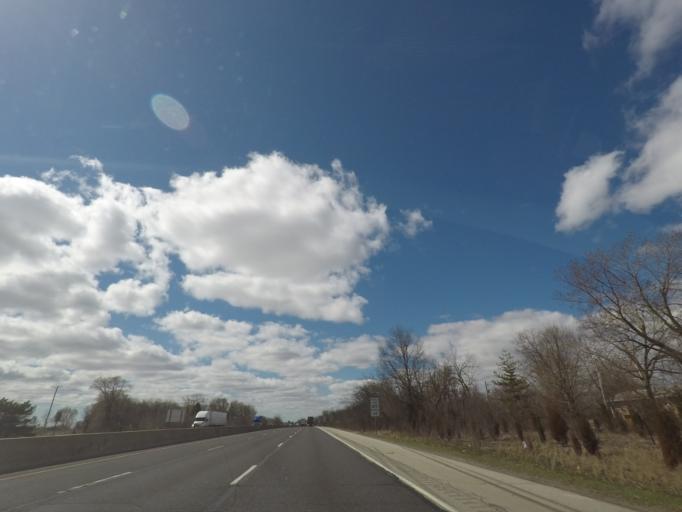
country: US
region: Illinois
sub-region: Will County
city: Shorewood
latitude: 41.5152
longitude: -88.1935
